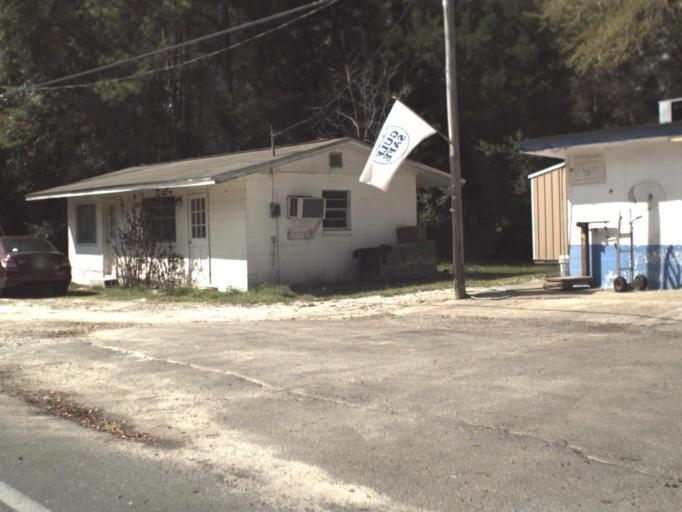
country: US
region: Florida
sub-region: Wakulla County
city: Crawfordville
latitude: 30.0767
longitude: -84.4135
